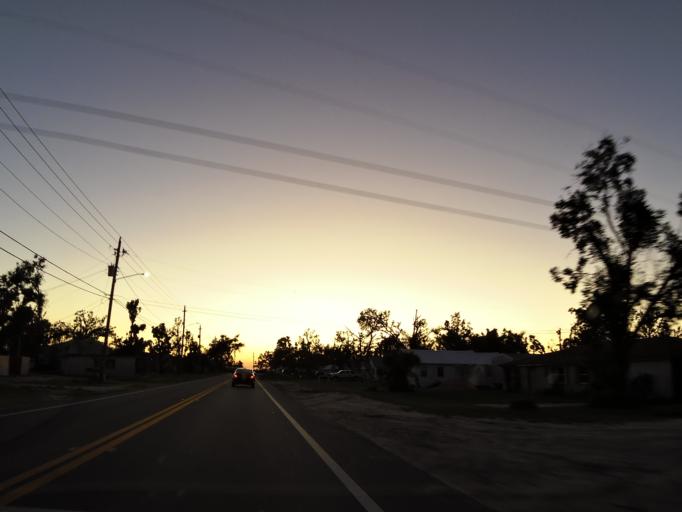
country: US
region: Florida
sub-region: Bay County
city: Parker
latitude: 30.1311
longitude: -85.6094
